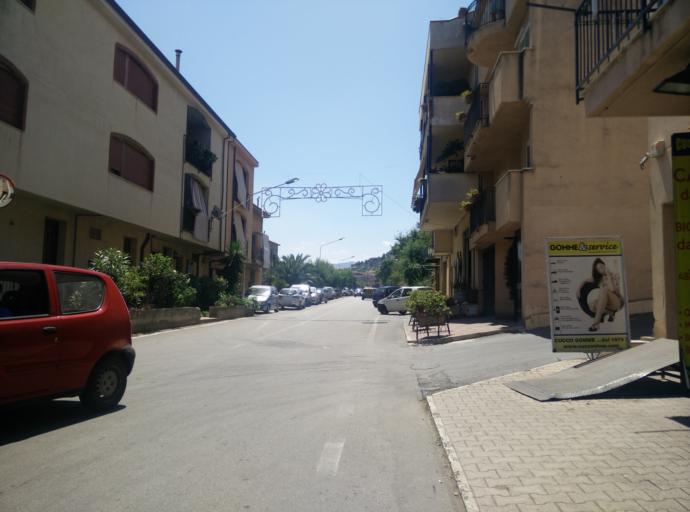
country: IT
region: Sicily
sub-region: Palermo
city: Castelbuono
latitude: 37.9306
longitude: 14.0906
